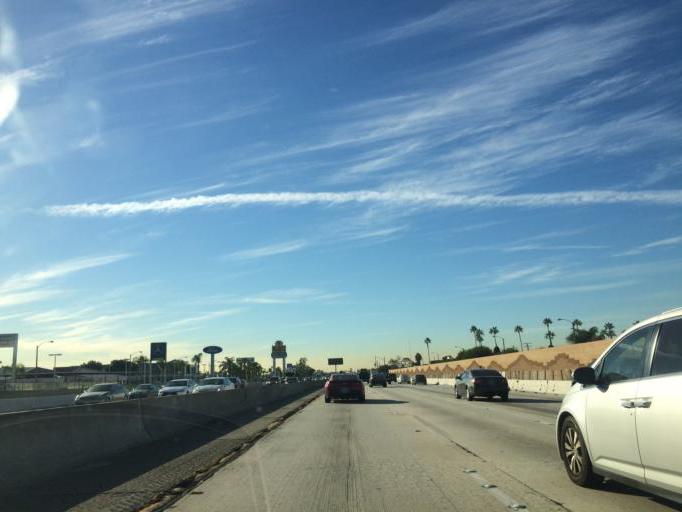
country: US
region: California
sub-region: Los Angeles County
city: Covina
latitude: 34.0721
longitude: -117.9006
